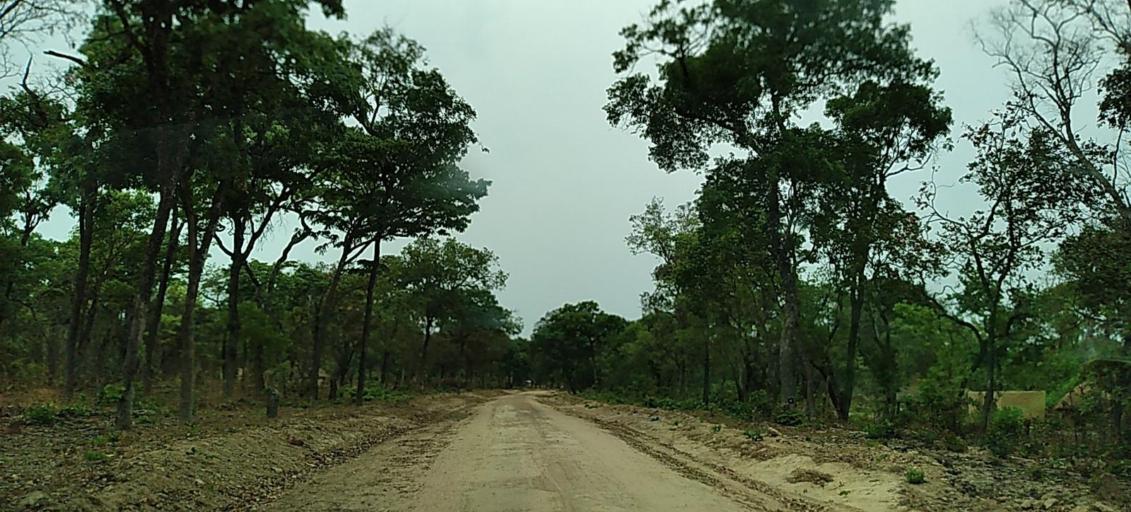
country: ZM
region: North-Western
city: Solwezi
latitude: -12.5426
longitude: 26.5271
